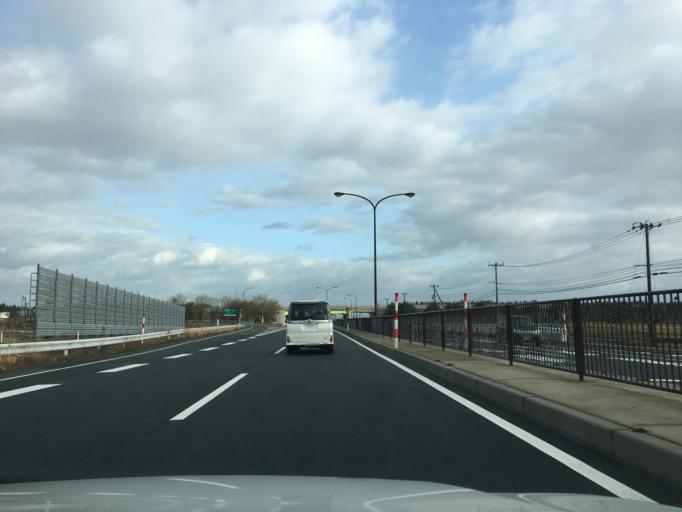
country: JP
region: Yamagata
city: Sakata
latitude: 38.8666
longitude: 139.8427
